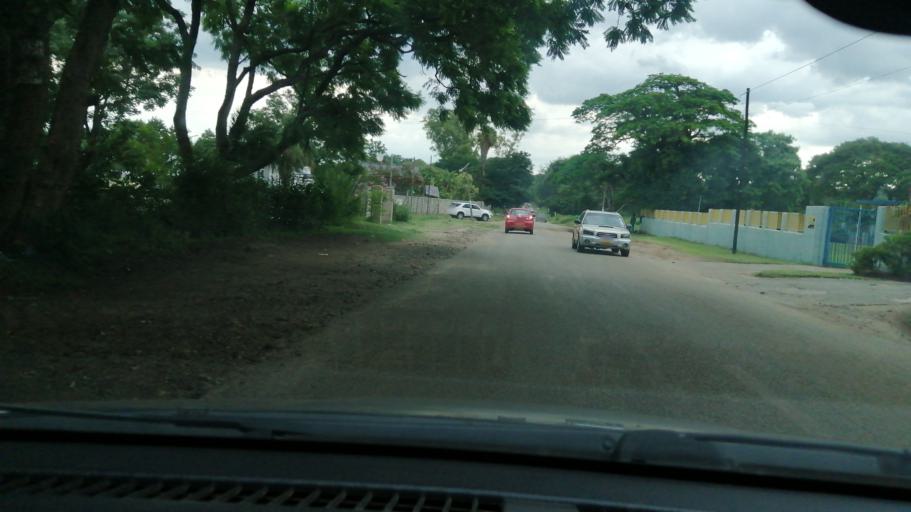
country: ZW
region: Harare
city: Harare
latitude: -17.7991
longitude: 31.0405
